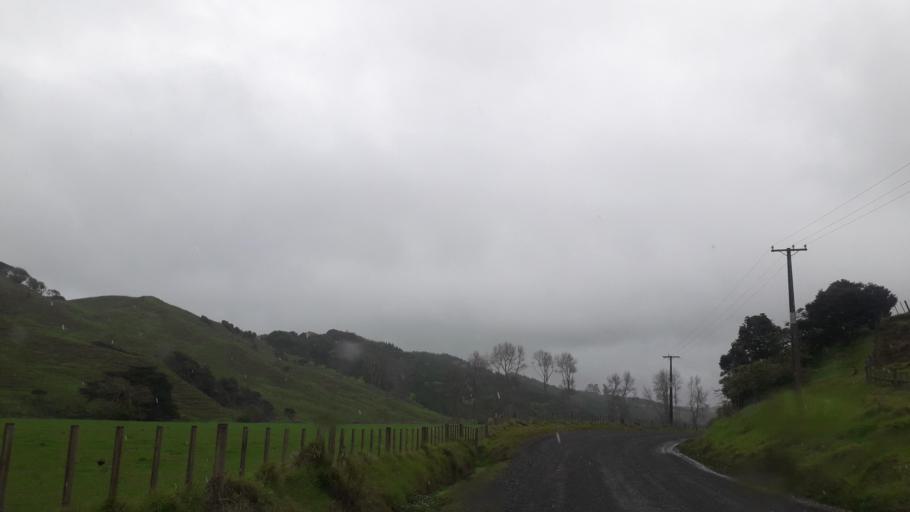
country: NZ
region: Northland
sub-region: Far North District
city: Ahipara
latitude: -35.4228
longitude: 173.3597
